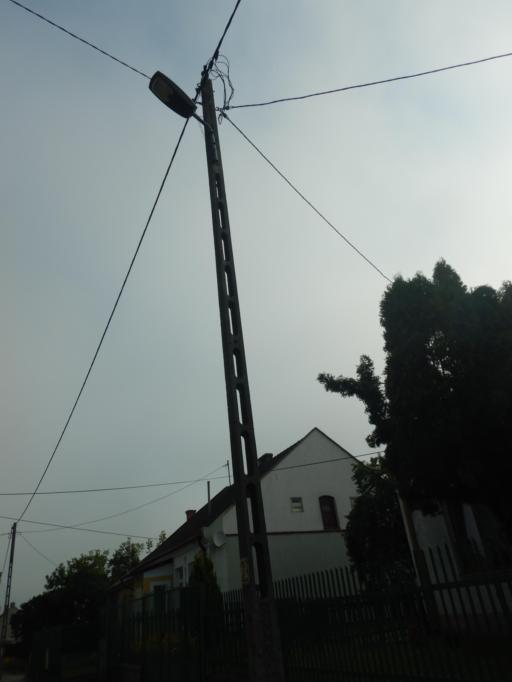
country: PL
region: Swietokrzyskie
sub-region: Powiat ostrowiecki
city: Cmielow
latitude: 50.8893
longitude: 21.5095
